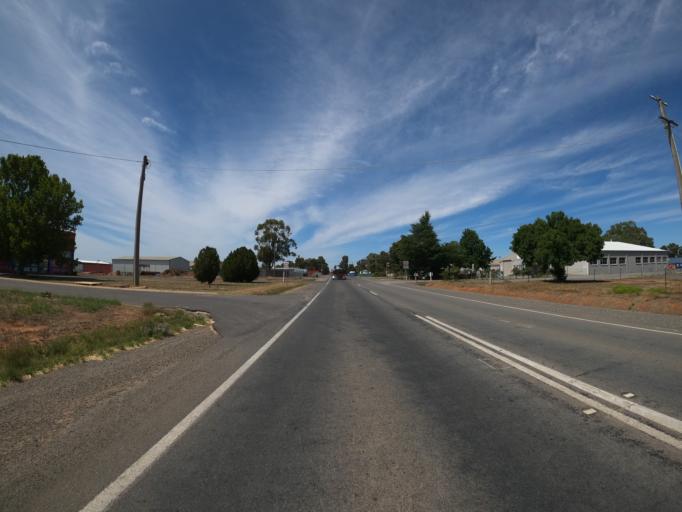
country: AU
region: Victoria
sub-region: Moira
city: Yarrawonga
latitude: -36.0282
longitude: 145.9955
